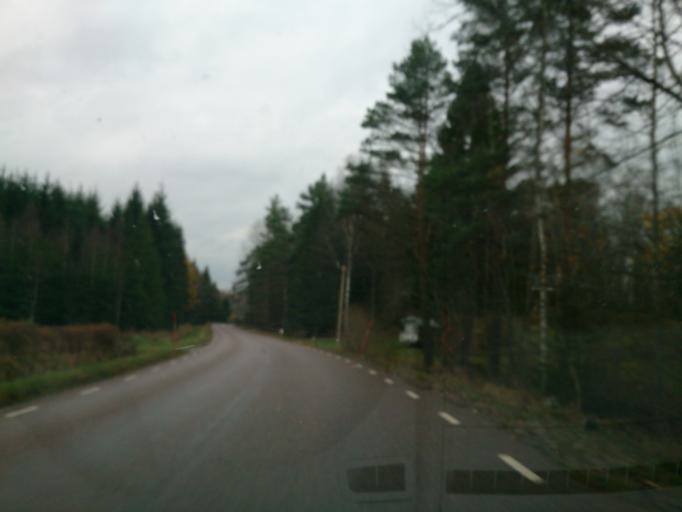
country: SE
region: OEstergoetland
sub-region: Atvidabergs Kommun
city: Atvidaberg
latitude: 58.3093
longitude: 16.0243
